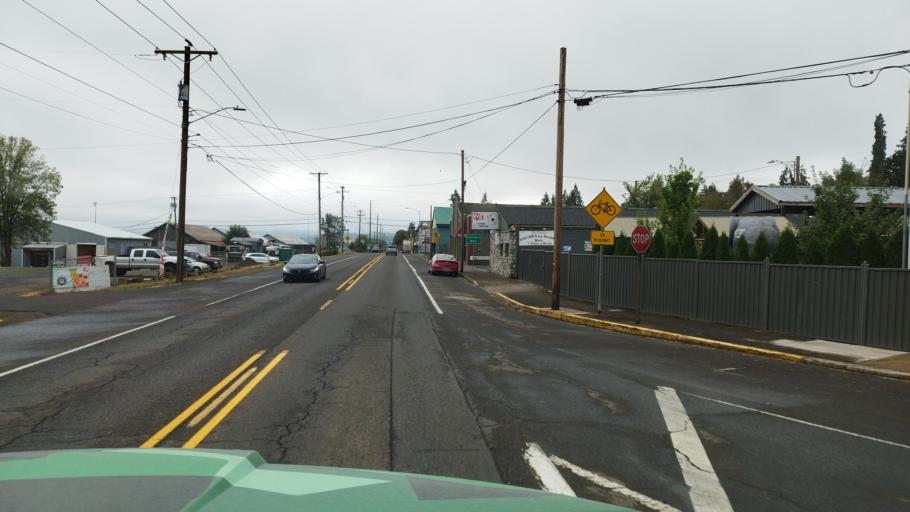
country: US
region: Oregon
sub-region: Washington County
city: Forest Grove
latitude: 45.4386
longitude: -123.1402
